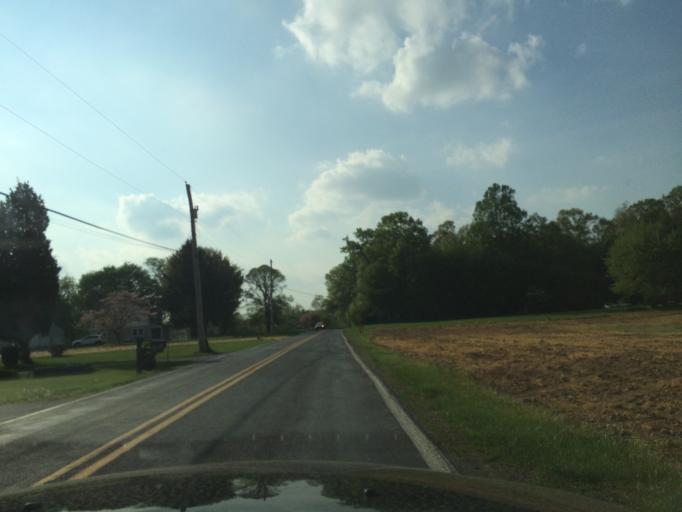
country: US
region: Maryland
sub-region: Carroll County
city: Mount Airy
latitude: 39.3015
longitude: -77.0969
